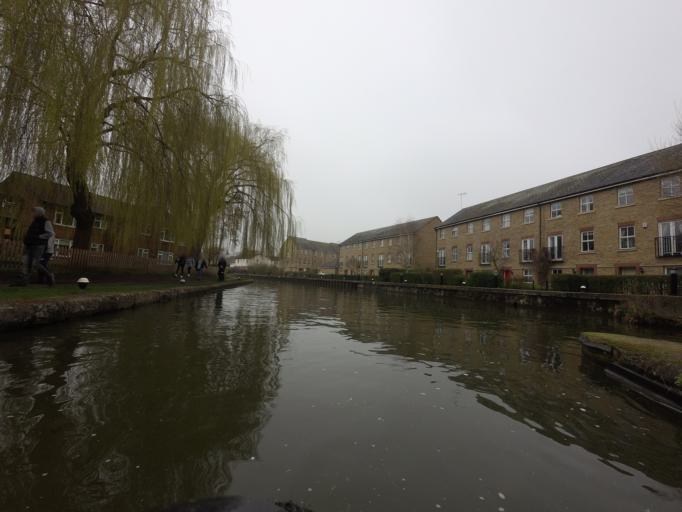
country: GB
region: England
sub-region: Hertfordshire
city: Berkhamsted
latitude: 51.7590
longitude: -0.5562
